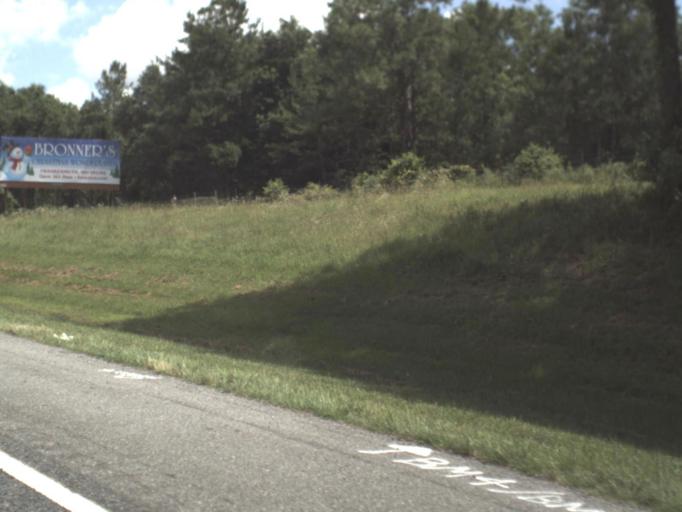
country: US
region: Florida
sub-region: Columbia County
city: Five Points
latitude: 30.2174
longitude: -82.7079
